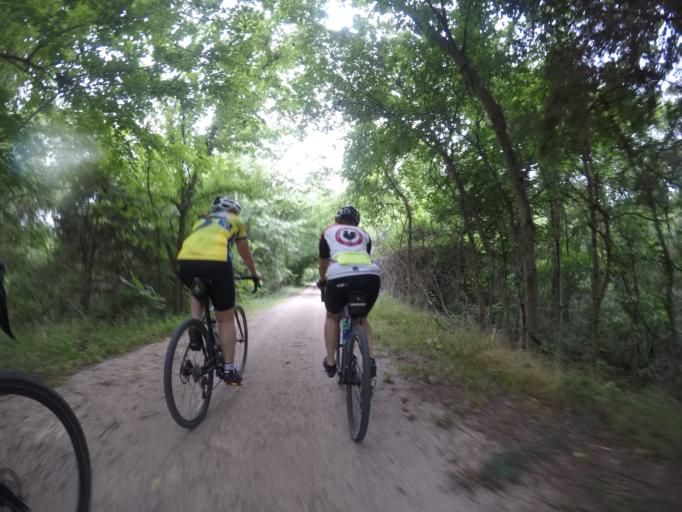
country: US
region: Kansas
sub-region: Anderson County
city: Garnett
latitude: 38.2400
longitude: -95.2593
